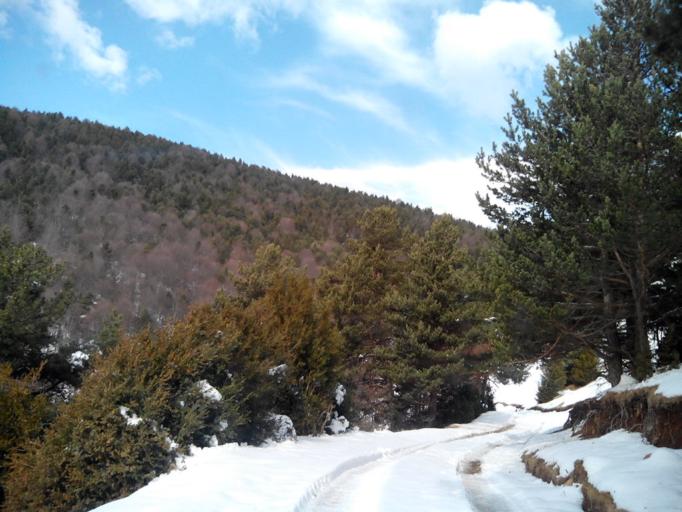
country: ES
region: Catalonia
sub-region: Provincia de Barcelona
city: Sant Julia de Cerdanyola
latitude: 42.1974
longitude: 1.9415
